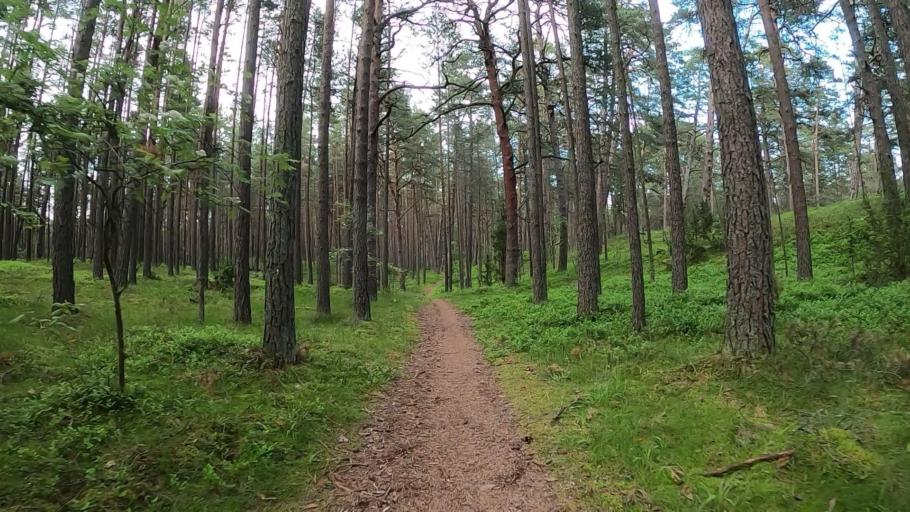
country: LV
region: Carnikava
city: Carnikava
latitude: 57.1201
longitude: 24.2075
